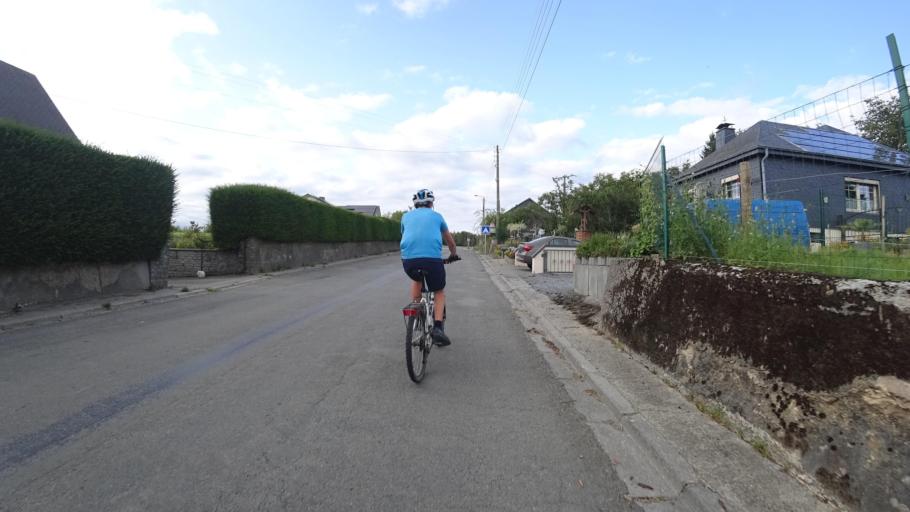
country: BE
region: Wallonia
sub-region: Province du Luxembourg
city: Bertrix
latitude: 49.8343
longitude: 5.3407
